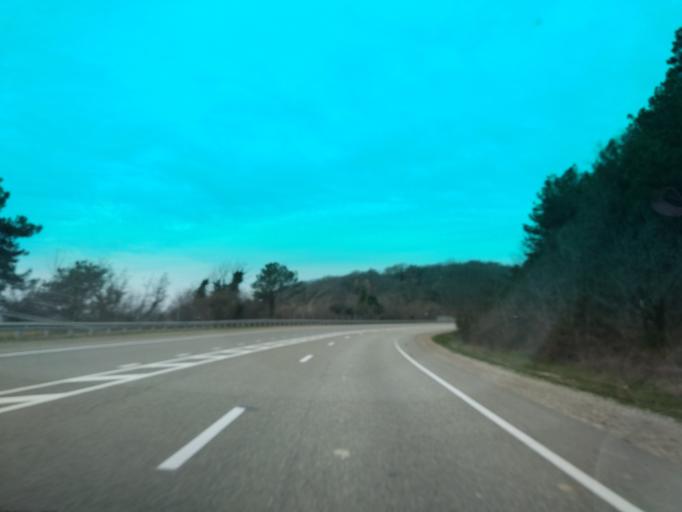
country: RU
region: Krasnodarskiy
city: Ol'ginka
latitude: 44.1868
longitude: 38.8942
